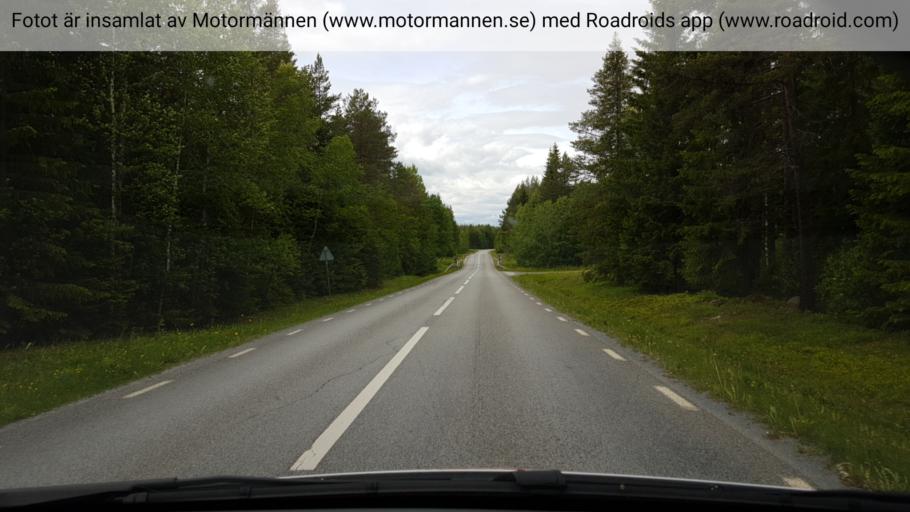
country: SE
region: Jaemtland
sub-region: Krokoms Kommun
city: Krokom
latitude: 63.1284
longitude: 14.2274
